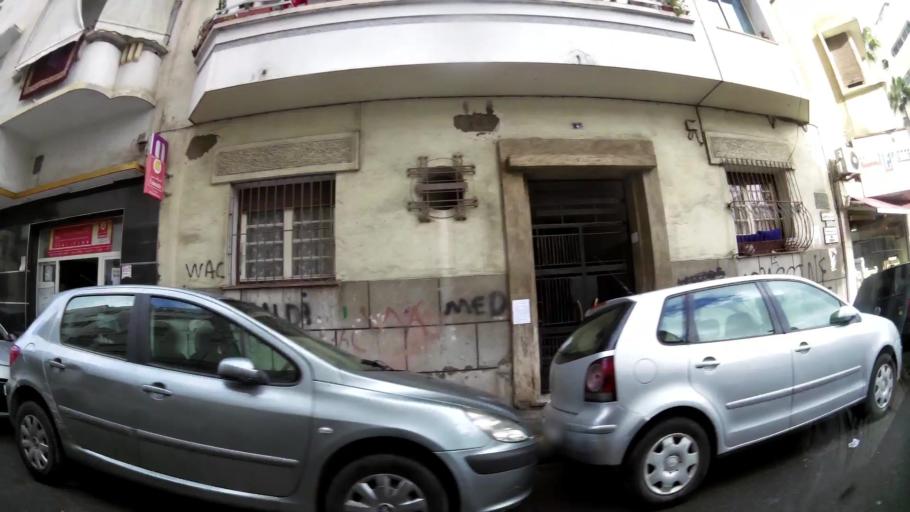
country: MA
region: Grand Casablanca
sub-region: Casablanca
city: Casablanca
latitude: 33.5862
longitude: -7.6152
